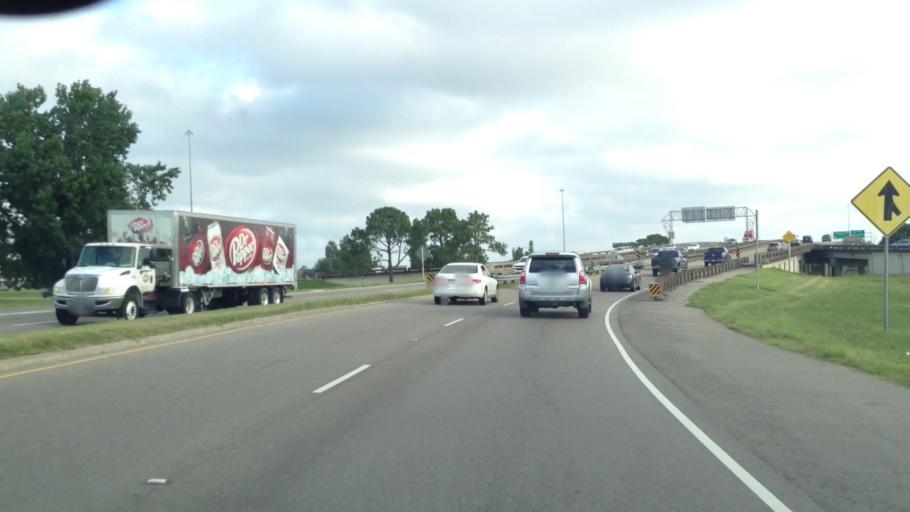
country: US
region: Louisiana
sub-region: Jefferson Parish
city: Metairie Terrace
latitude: 29.9963
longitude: -90.1835
